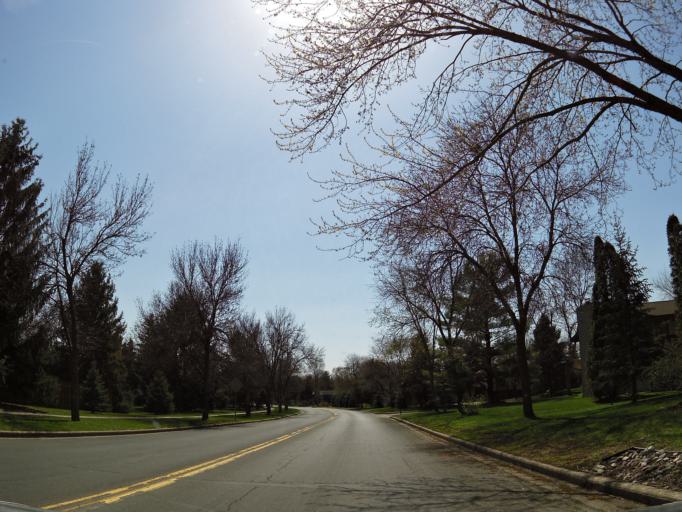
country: US
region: Wisconsin
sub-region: Saint Croix County
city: Hudson
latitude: 44.9683
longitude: -92.7343
